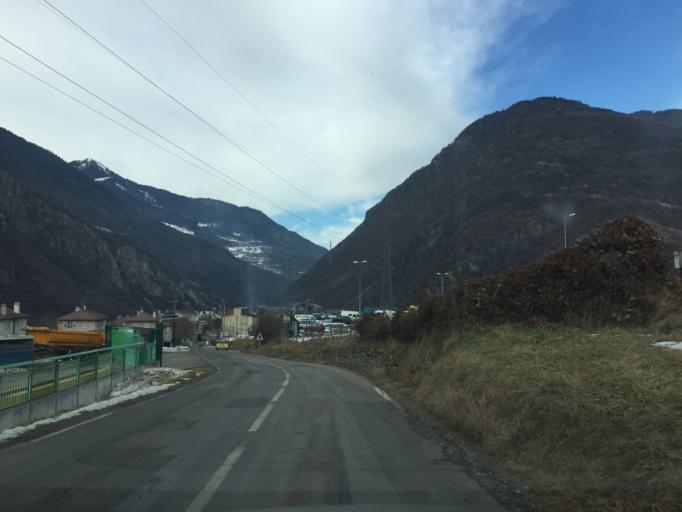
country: FR
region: Rhone-Alpes
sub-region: Departement de la Savoie
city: Aigueblanche
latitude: 45.5178
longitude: 6.4892
